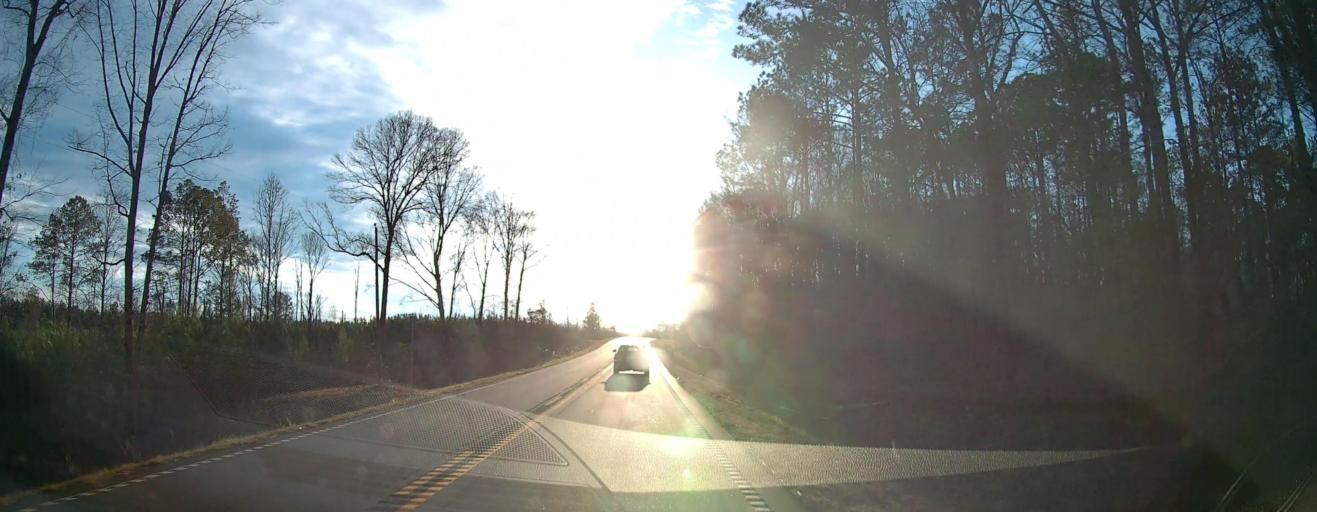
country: US
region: Georgia
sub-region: Talbot County
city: Sardis
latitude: 32.7222
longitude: -84.6488
